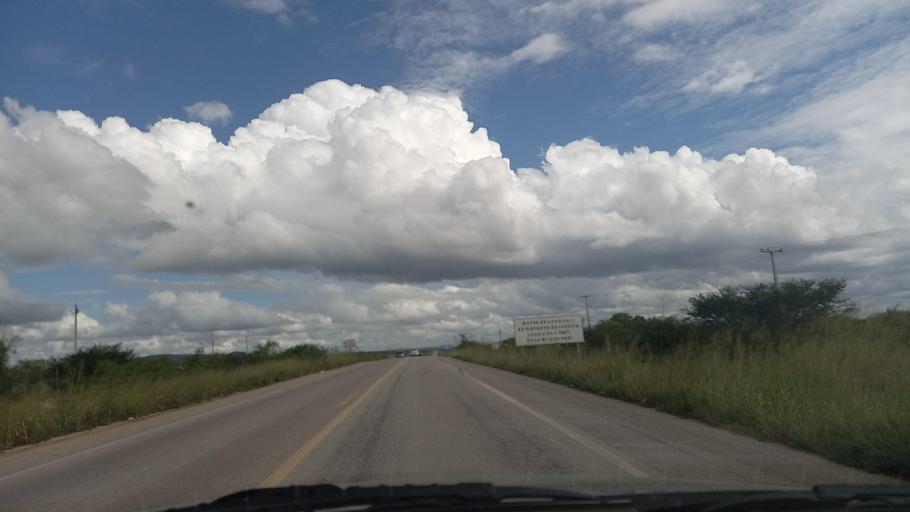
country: BR
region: Pernambuco
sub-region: Cachoeirinha
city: Cachoeirinha
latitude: -8.4780
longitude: -36.2232
